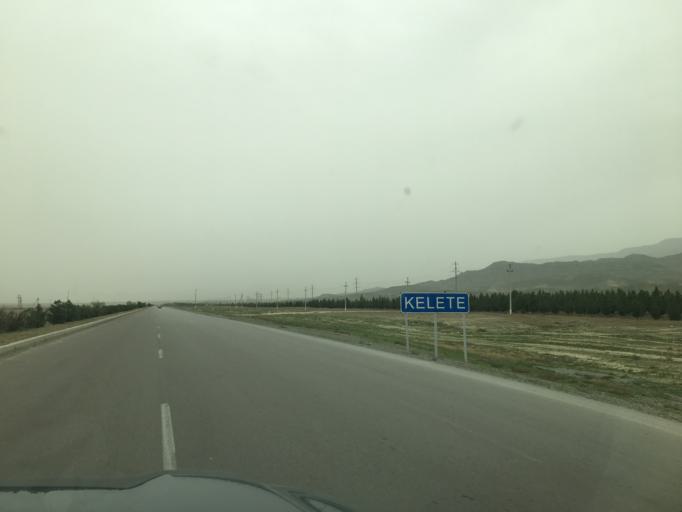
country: TM
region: Ahal
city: Baharly
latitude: 38.2735
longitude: 57.6937
